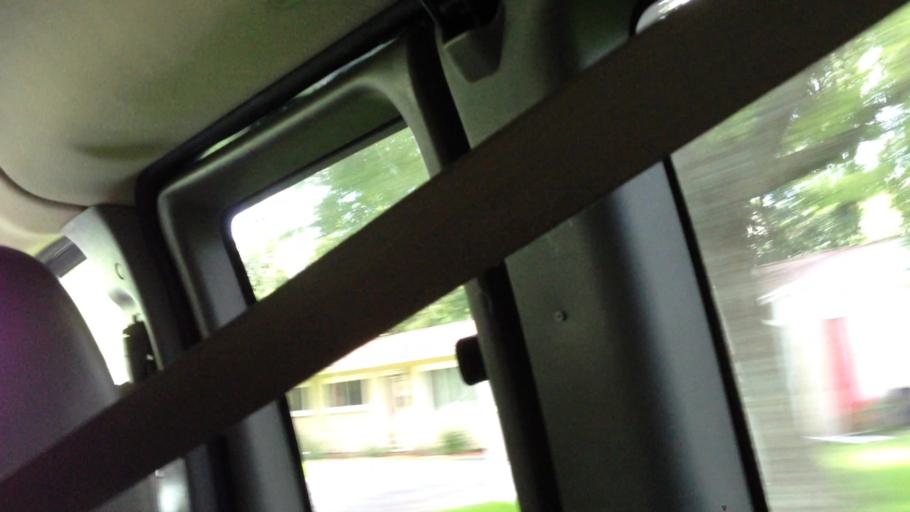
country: US
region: New York
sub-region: Dutchess County
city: Red Hook
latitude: 42.0208
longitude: -73.8844
